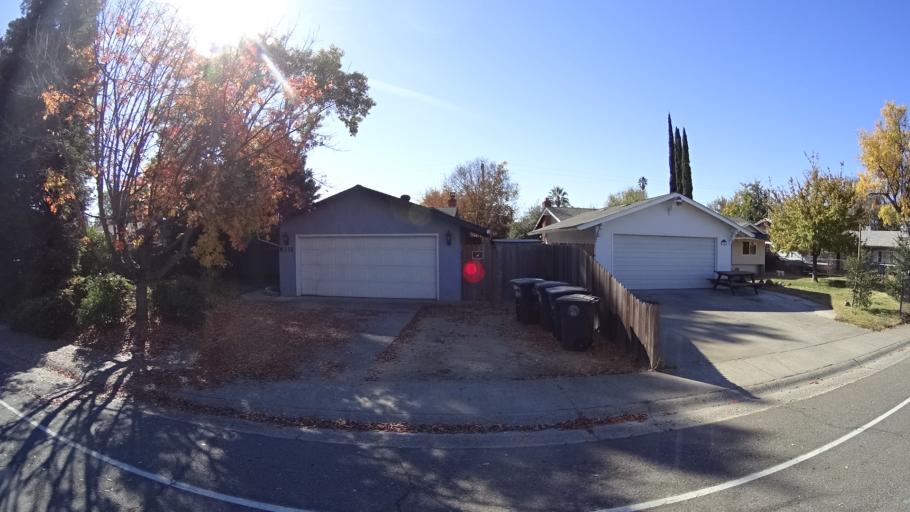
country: US
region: California
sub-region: Sacramento County
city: Antelope
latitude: 38.7172
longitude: -121.3075
